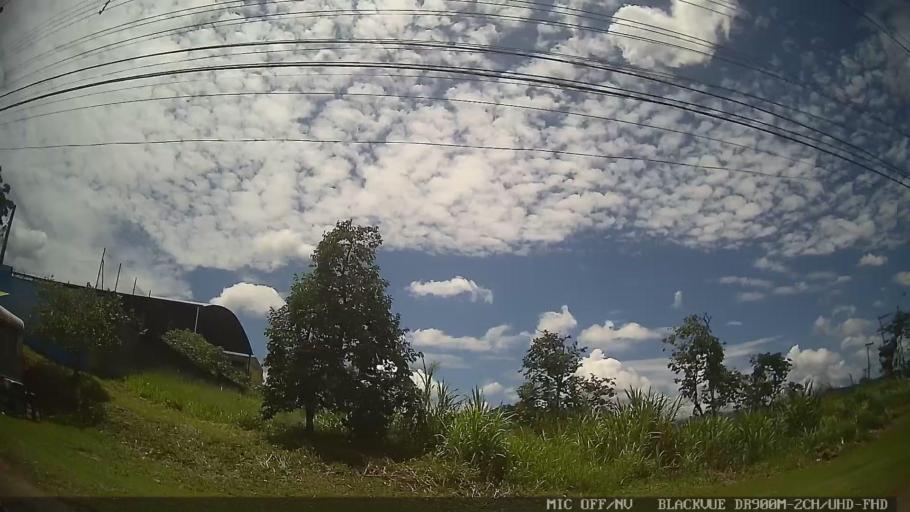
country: BR
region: Sao Paulo
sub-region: Biritiba-Mirim
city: Biritiba Mirim
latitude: -23.5802
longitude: -46.0396
